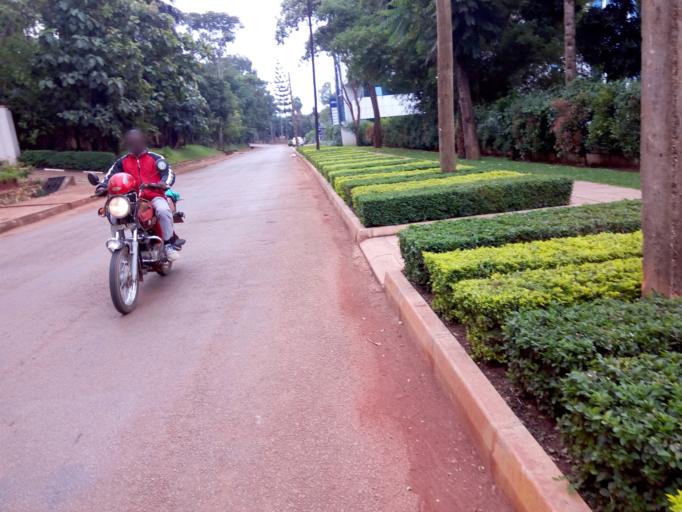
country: UG
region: Central Region
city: Kampala Central Division
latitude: 0.3255
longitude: 32.5825
